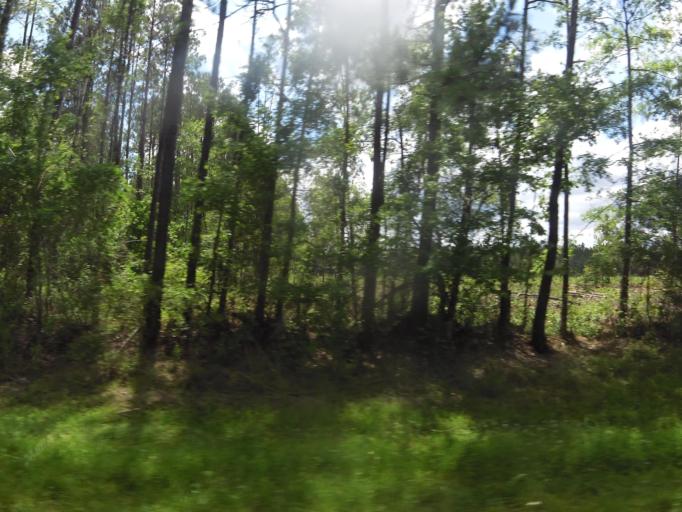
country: US
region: Florida
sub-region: Clay County
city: Green Cove Springs
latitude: 29.9928
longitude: -81.7314
